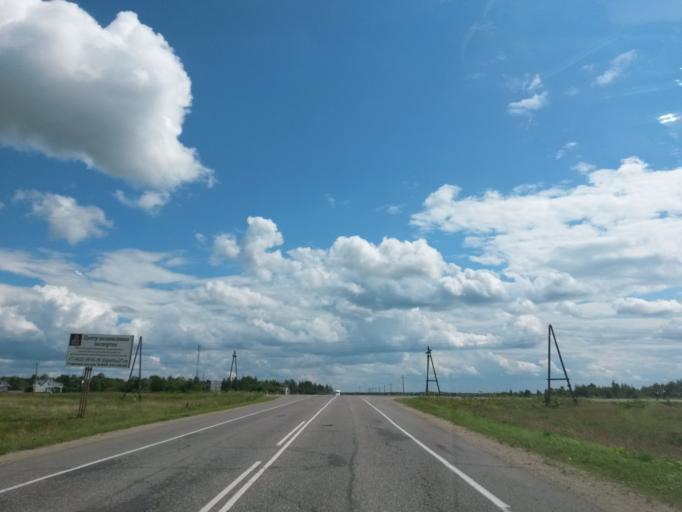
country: RU
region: Ivanovo
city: Pistsovo
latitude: 57.1752
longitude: 40.5011
